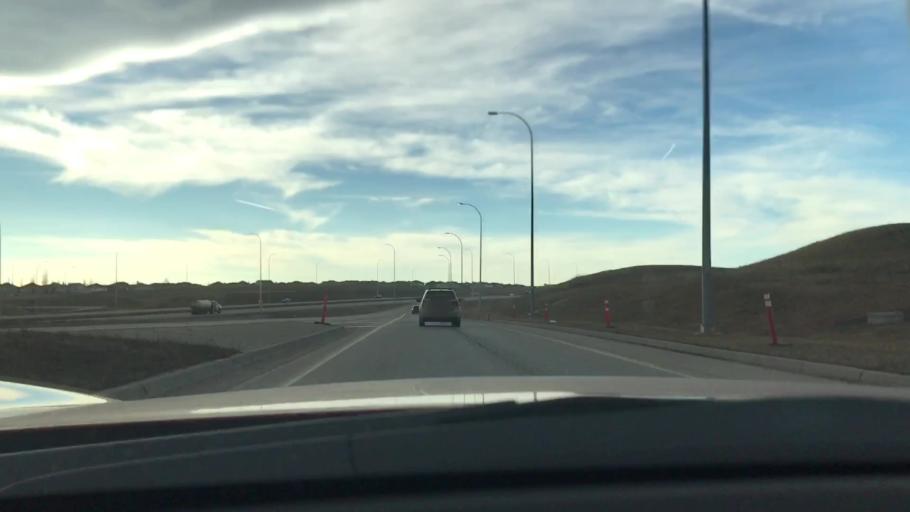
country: CA
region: Alberta
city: Calgary
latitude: 51.1531
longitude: -114.1663
